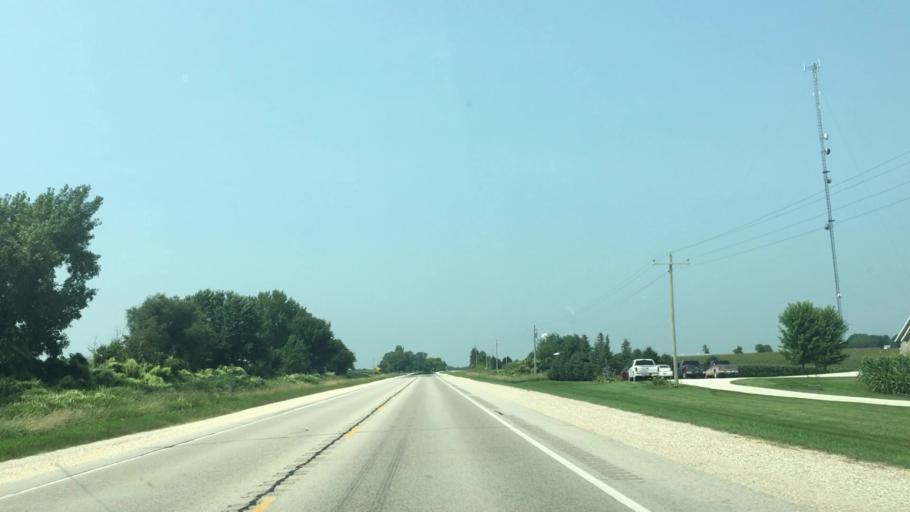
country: US
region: Iowa
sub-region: Winneshiek County
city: Decorah
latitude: 43.1988
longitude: -91.8750
